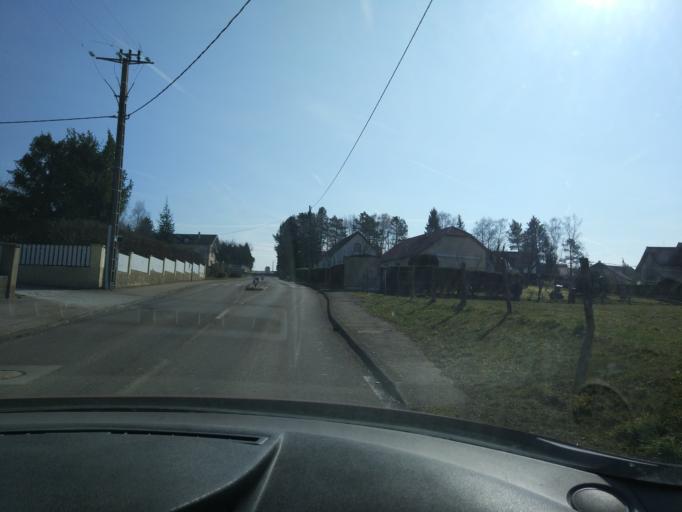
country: FR
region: Franche-Comte
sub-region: Departement du Doubs
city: Saone
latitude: 47.2205
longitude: 6.1239
